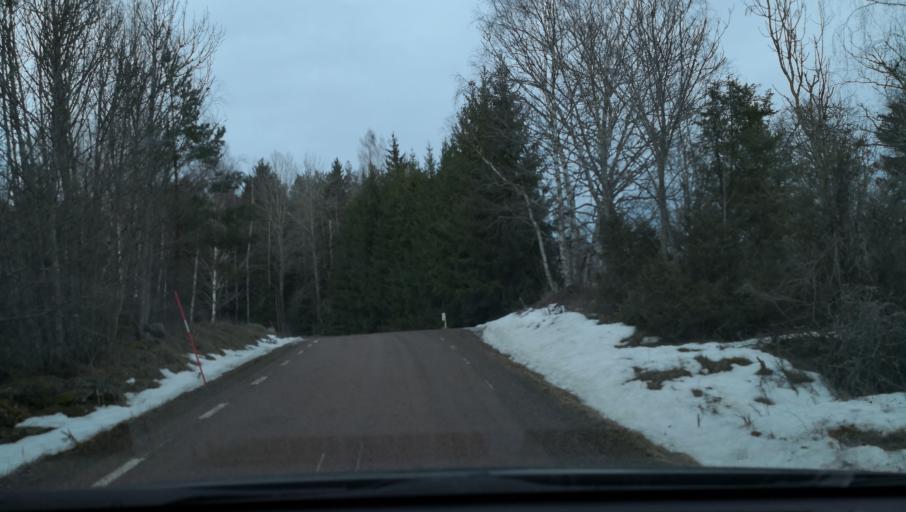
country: SE
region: Vaestmanland
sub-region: Vasteras
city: Skultuna
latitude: 59.6269
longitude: 16.4138
